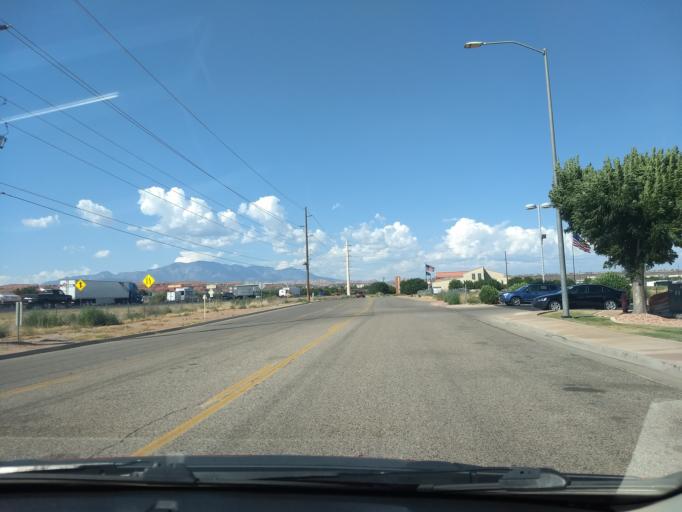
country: US
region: Utah
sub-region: Washington County
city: Saint George
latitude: 37.0855
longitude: -113.5806
